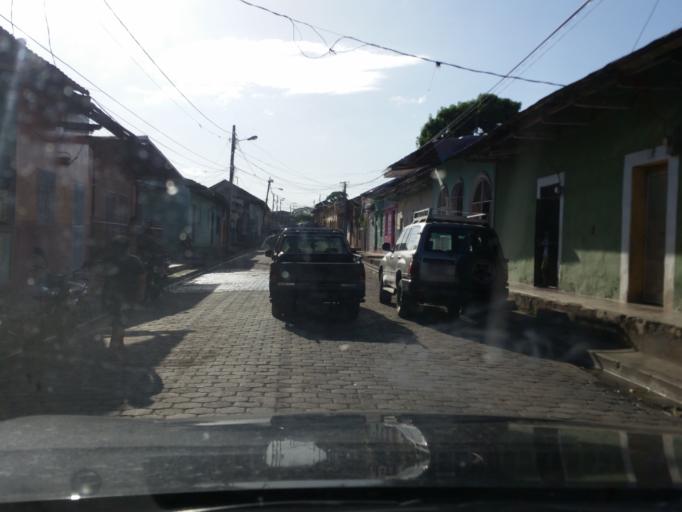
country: NI
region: Granada
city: Granada
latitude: 11.9250
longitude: -85.9609
